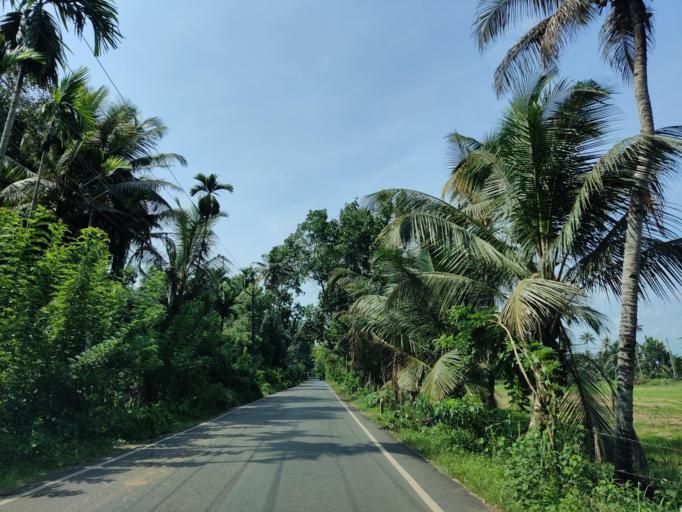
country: IN
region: Kerala
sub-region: Alappuzha
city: Mavelikara
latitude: 9.3338
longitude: 76.4683
